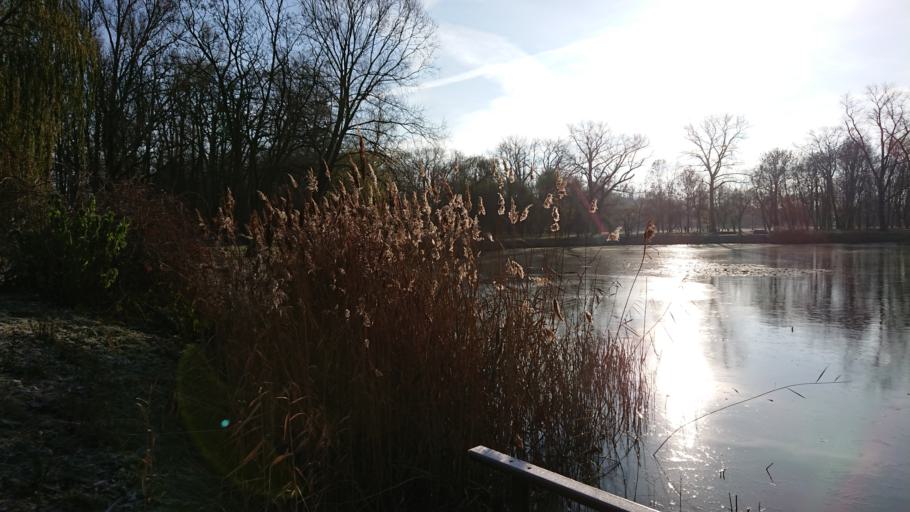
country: PL
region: Kujawsko-Pomorskie
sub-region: Powiat inowroclawski
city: Inowroclaw
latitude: 52.7926
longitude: 18.2414
